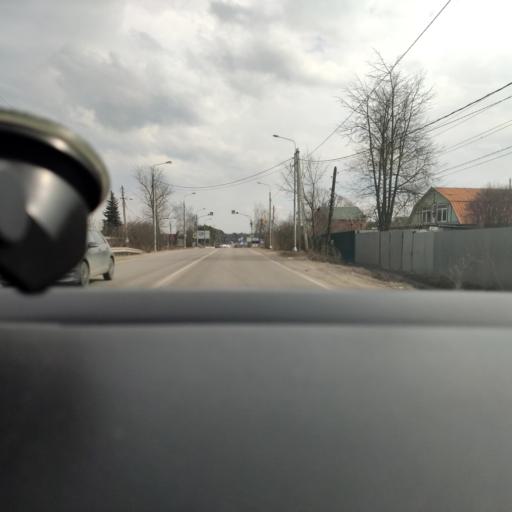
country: RU
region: Moskovskaya
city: Bykovo
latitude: 55.6560
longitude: 38.1080
